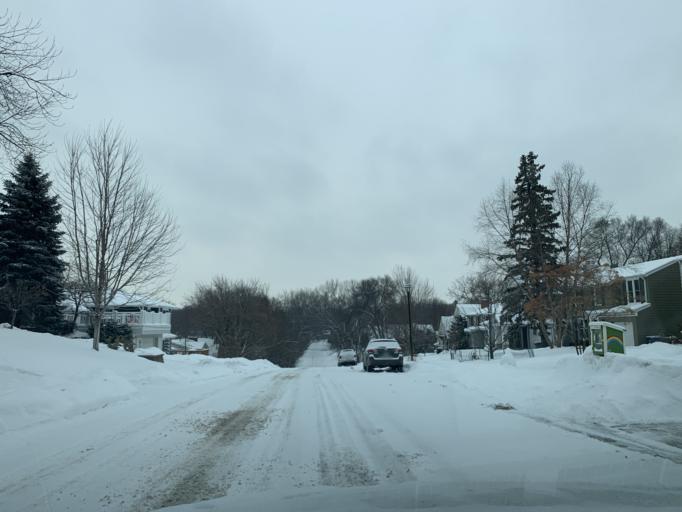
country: US
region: Minnesota
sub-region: Hennepin County
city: Saint Louis Park
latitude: 44.9301
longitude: -93.3367
